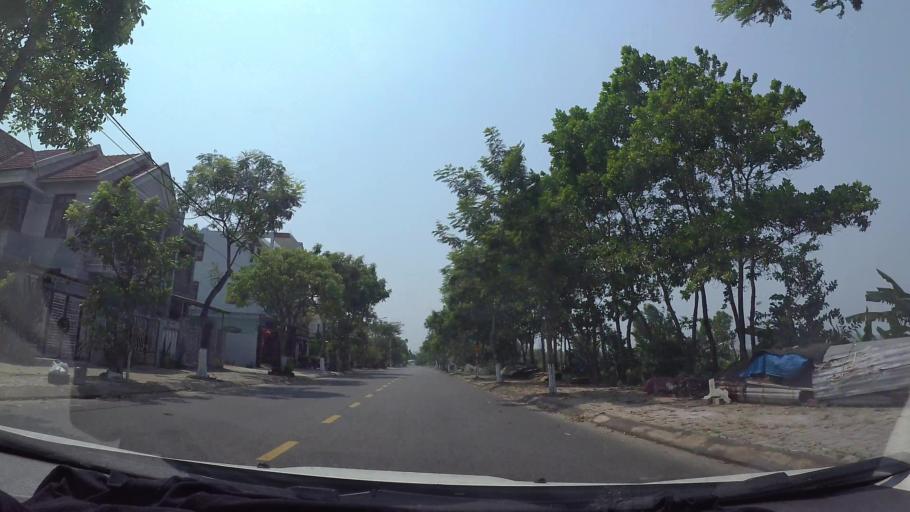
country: VN
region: Da Nang
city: Cam Le
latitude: 15.9975
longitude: 108.1990
